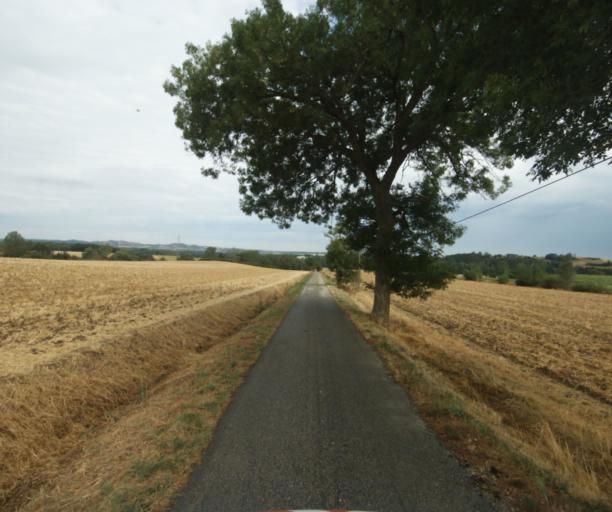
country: FR
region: Midi-Pyrenees
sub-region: Departement de la Haute-Garonne
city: Revel
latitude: 43.4163
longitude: 1.9717
